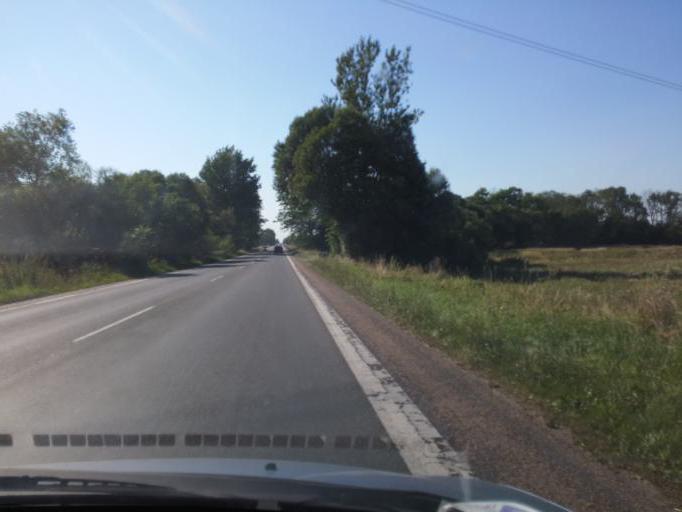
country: DK
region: South Denmark
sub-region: Odense Kommune
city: Bullerup
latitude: 55.3868
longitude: 10.5085
